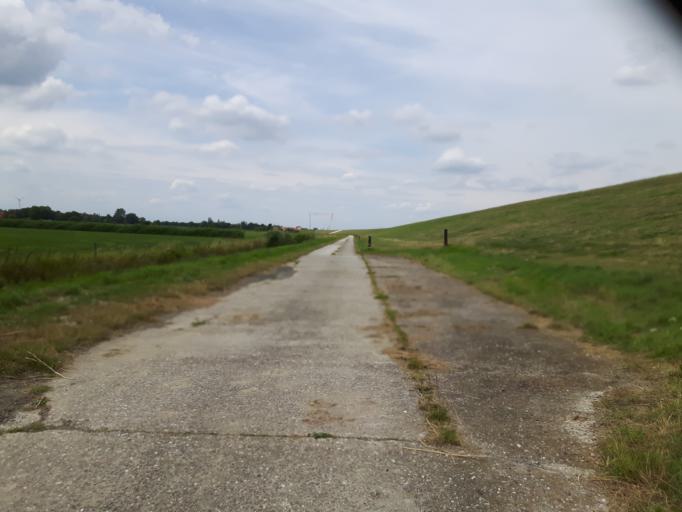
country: DE
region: Lower Saxony
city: Varel
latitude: 53.3904
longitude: 8.2244
